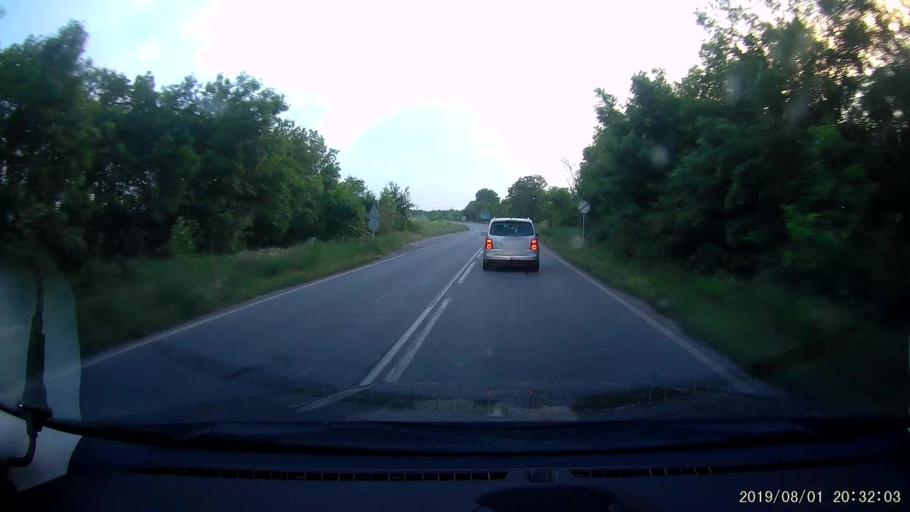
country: BG
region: Yambol
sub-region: Obshtina Elkhovo
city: Elkhovo
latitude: 42.1247
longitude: 26.5349
